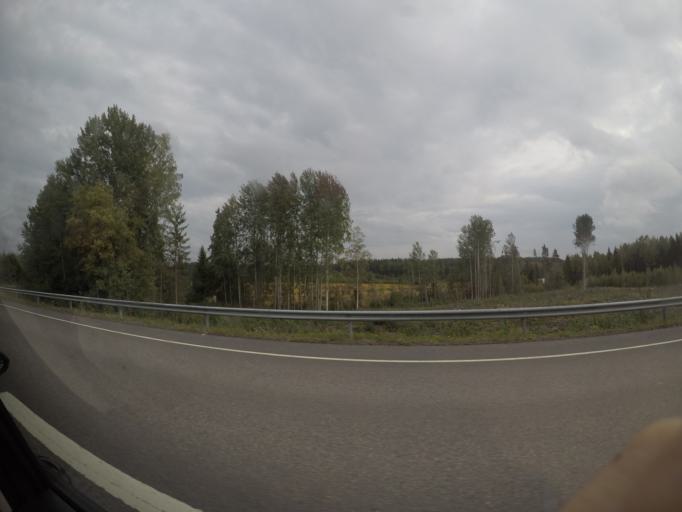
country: FI
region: Haeme
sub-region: Haemeenlinna
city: Parola
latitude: 61.0909
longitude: 24.4019
